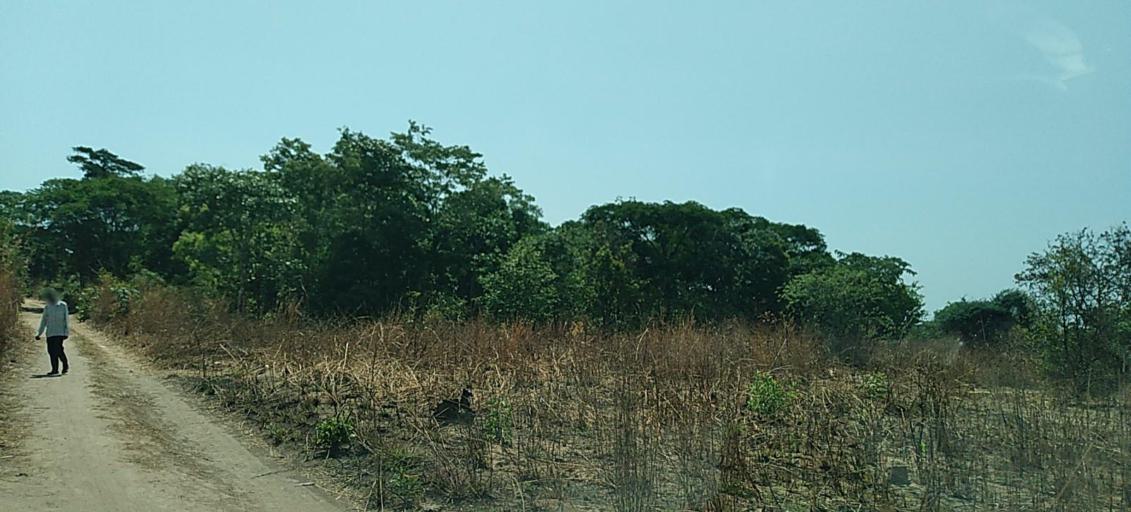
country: ZM
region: Copperbelt
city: Luanshya
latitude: -13.0069
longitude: 28.4763
